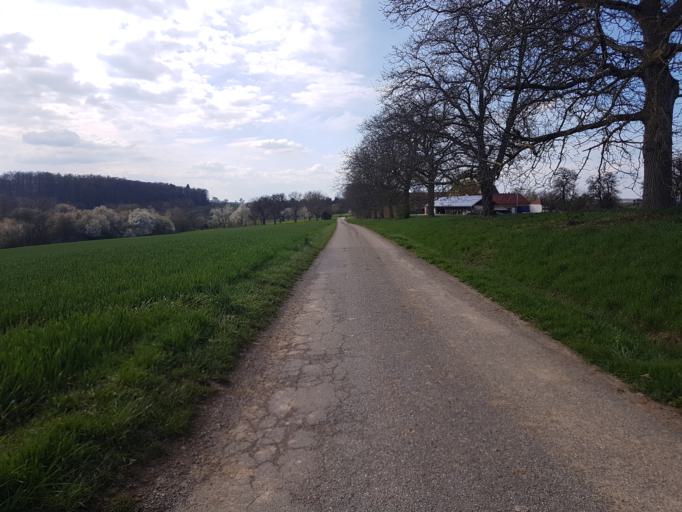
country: DE
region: Baden-Wuerttemberg
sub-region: Regierungsbezirk Stuttgart
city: Forchtenberg
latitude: 49.3293
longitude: 9.5408
